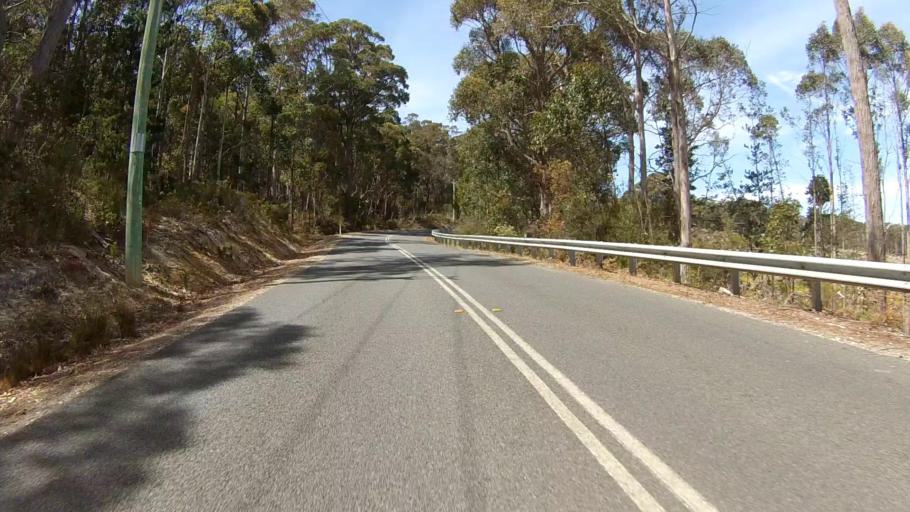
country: AU
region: Tasmania
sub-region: Huon Valley
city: Cygnet
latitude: -43.2222
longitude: 147.1279
